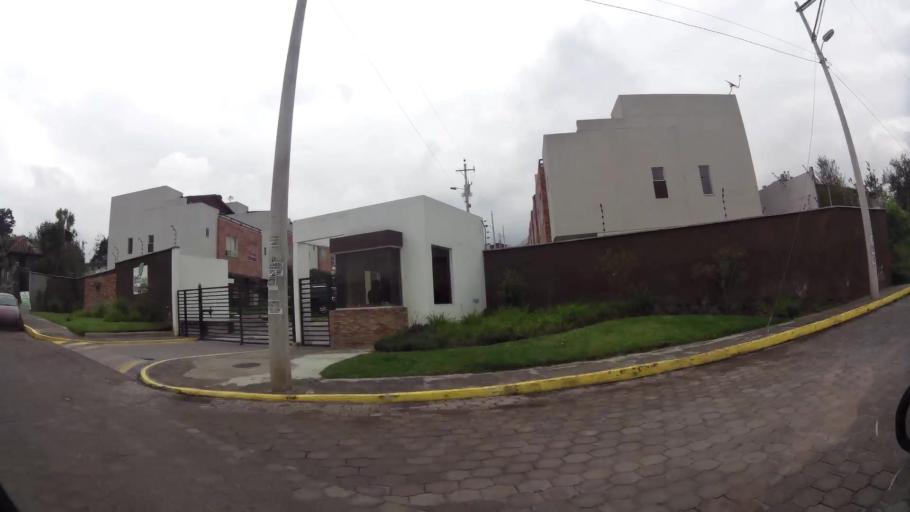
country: EC
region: Pichincha
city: Sangolqui
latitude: -0.3016
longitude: -78.4747
